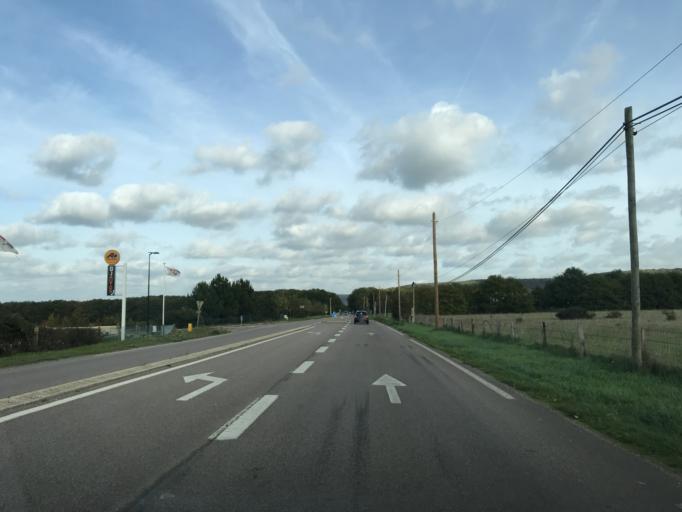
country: FR
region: Haute-Normandie
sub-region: Departement de l'Eure
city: Courcelles-sur-Seine
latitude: 49.1901
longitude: 1.3680
